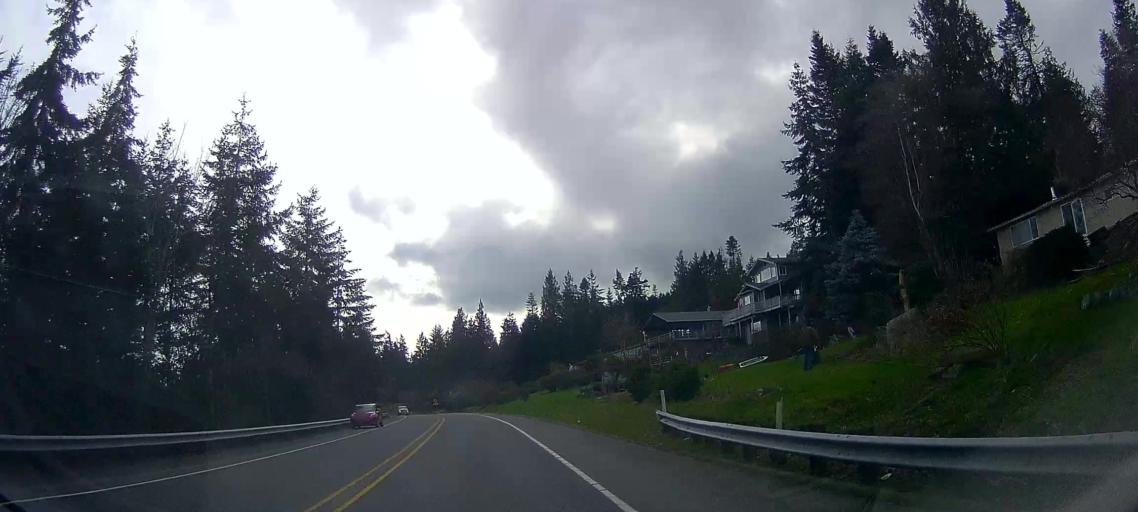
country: US
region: Washington
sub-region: Island County
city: Camano
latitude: 48.1851
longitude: -122.4807
